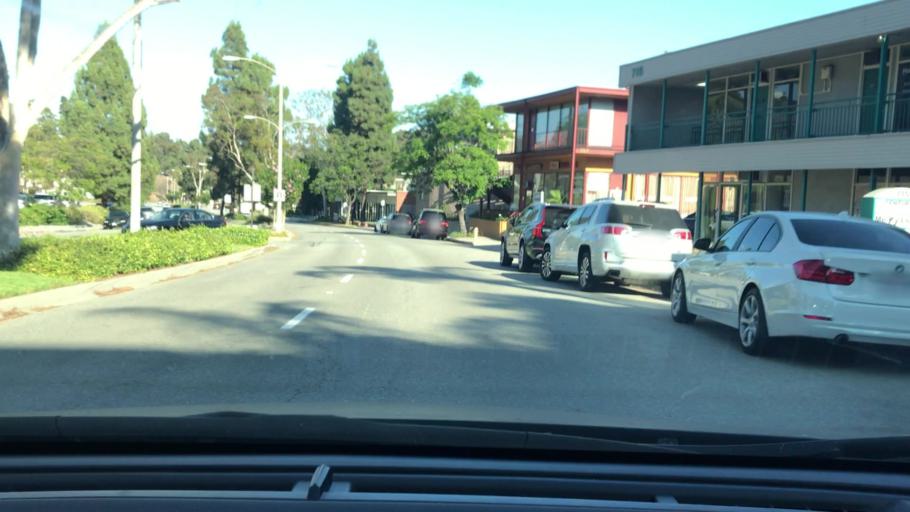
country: US
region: California
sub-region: Los Angeles County
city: Rolling Hills Estates
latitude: 33.7709
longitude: -118.3699
